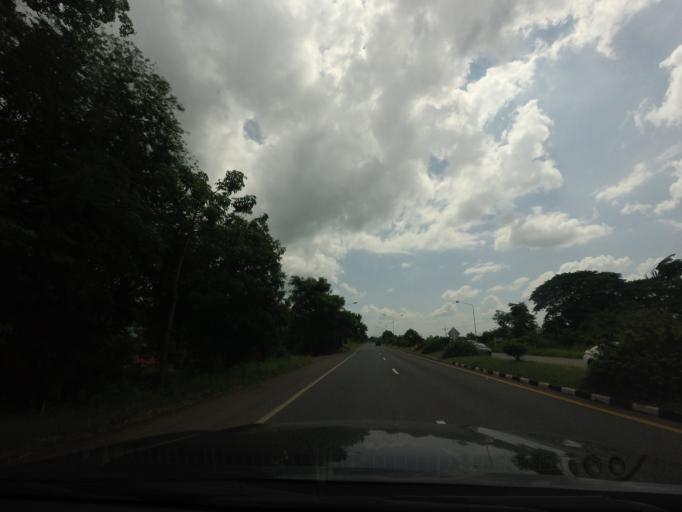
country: TH
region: Phetchabun
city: Nong Phai
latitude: 16.1903
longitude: 101.0889
